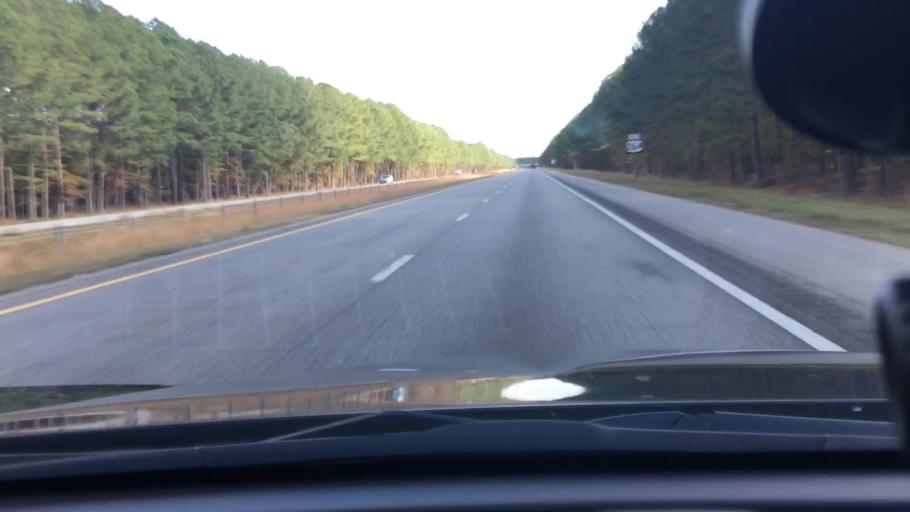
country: US
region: North Carolina
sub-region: Wilson County
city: Wilson
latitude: 35.6628
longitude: -77.7570
